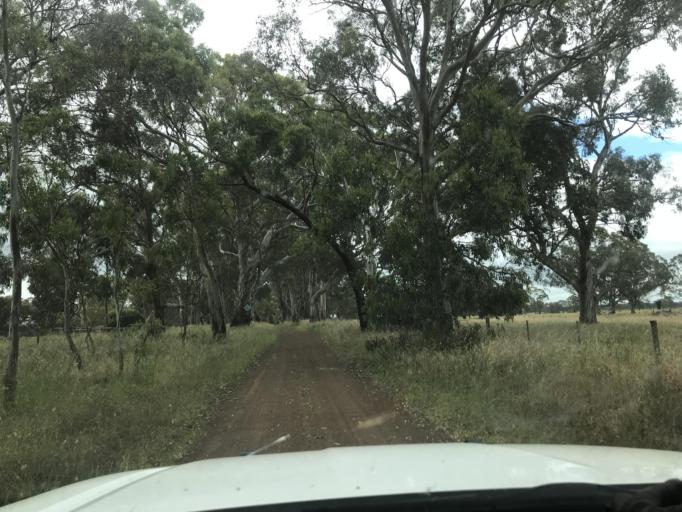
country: AU
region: South Australia
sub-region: Wattle Range
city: Penola
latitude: -37.0825
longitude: 141.2795
